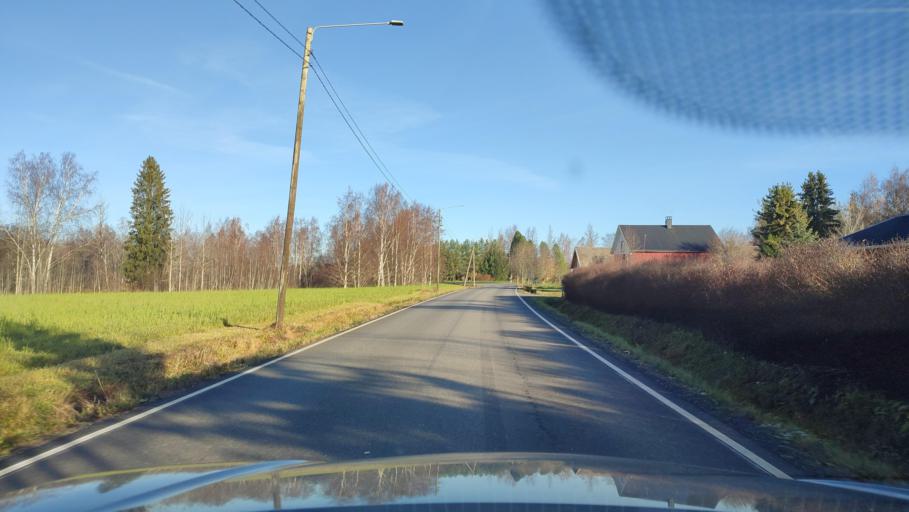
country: FI
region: Southern Ostrobothnia
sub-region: Suupohja
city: Karijoki
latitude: 62.2788
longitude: 21.7092
